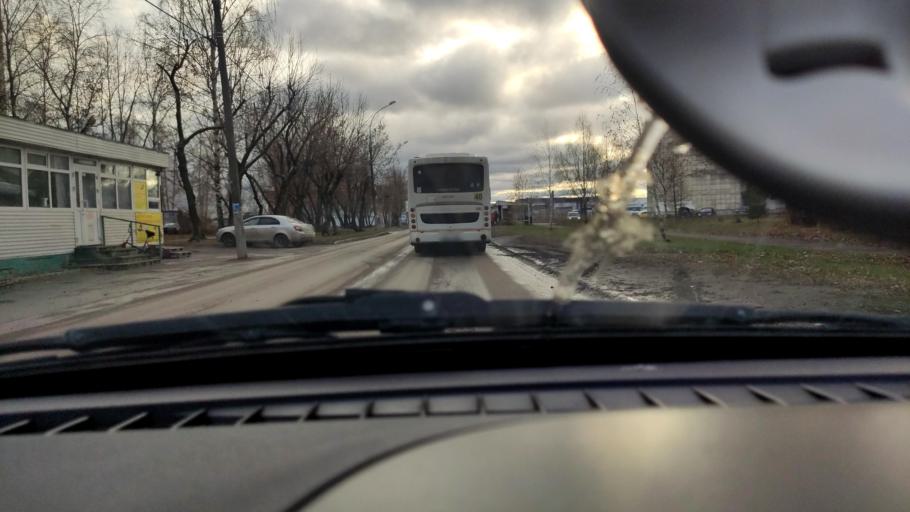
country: RU
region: Perm
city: Kondratovo
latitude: 57.9615
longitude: 56.1681
